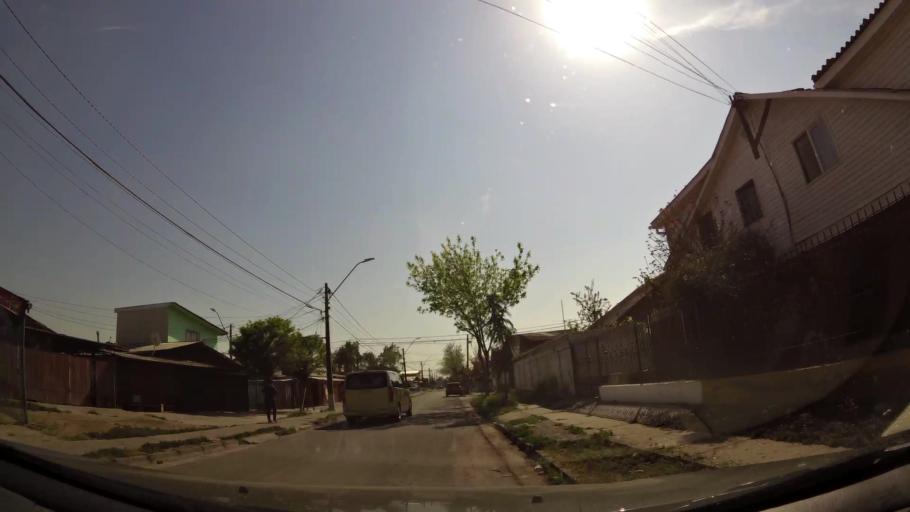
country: CL
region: Santiago Metropolitan
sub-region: Provincia de Maipo
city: San Bernardo
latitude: -33.5926
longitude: -70.6884
